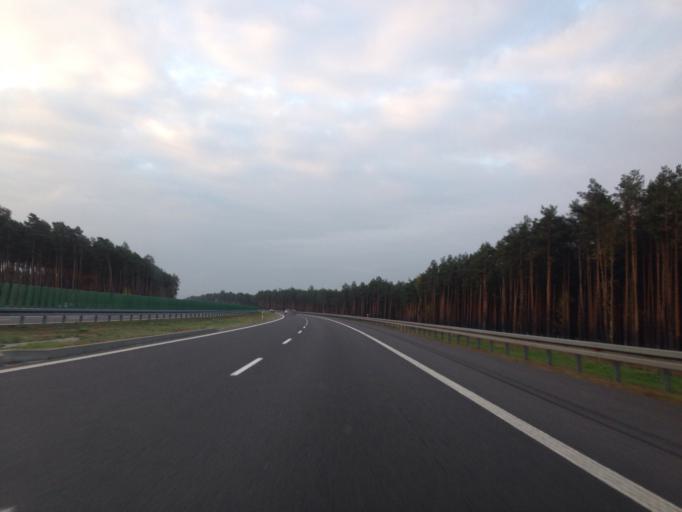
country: PL
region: Kujawsko-Pomorskie
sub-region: Powiat swiecki
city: Warlubie
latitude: 53.5269
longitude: 18.5993
